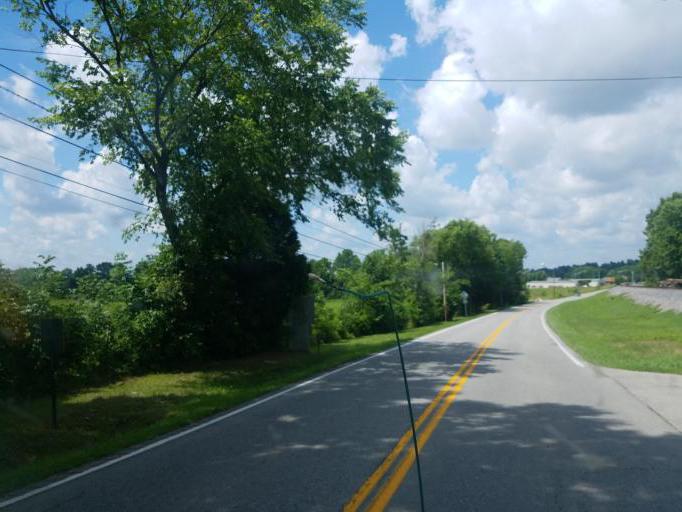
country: US
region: Kentucky
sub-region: Grayson County
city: Leitchfield
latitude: 37.4907
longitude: -86.2489
